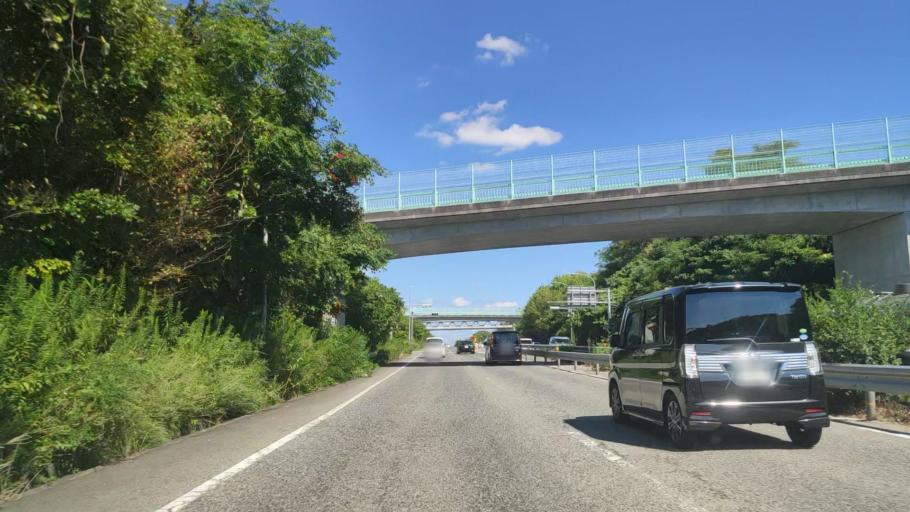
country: JP
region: Hyogo
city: Ono
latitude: 34.8483
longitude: 134.9499
